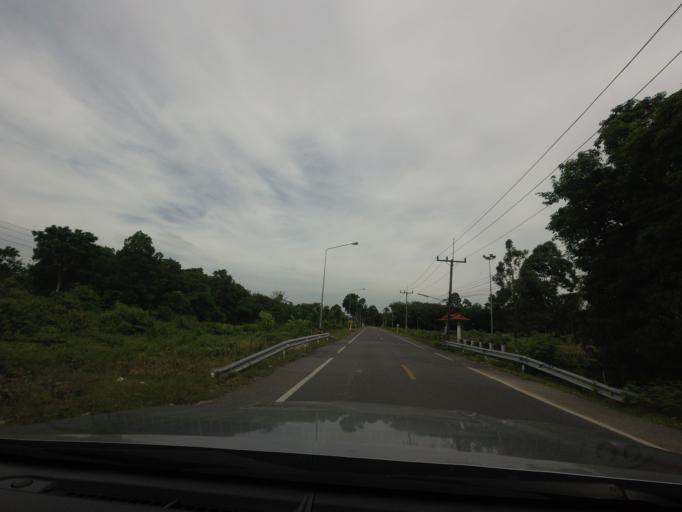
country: TH
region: Yala
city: Raman
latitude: 6.4508
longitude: 101.4504
